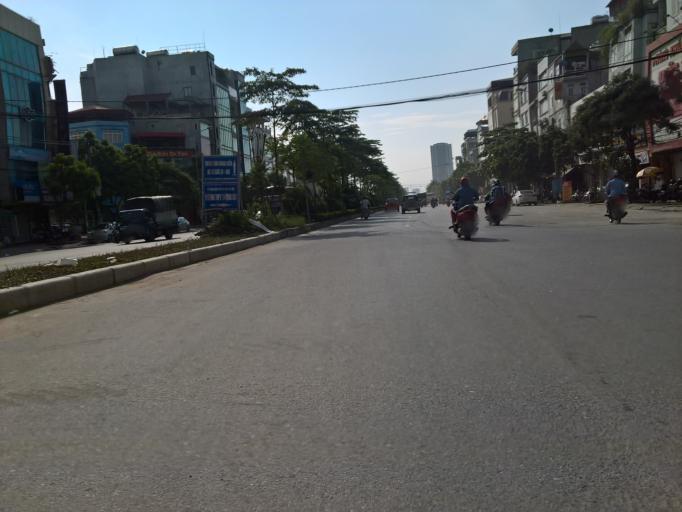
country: VN
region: Ha Noi
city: Troi
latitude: 21.0542
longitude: 105.7329
